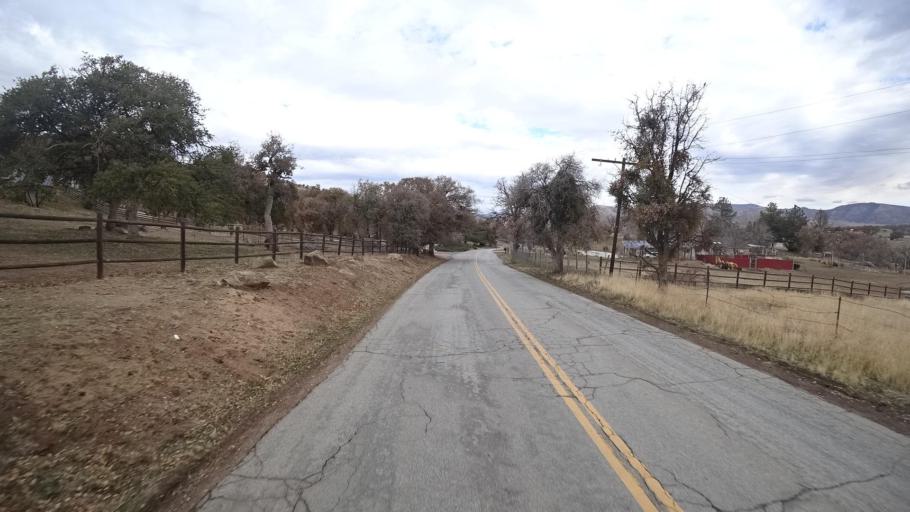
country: US
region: California
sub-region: Kern County
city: Golden Hills
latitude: 35.1146
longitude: -118.5149
